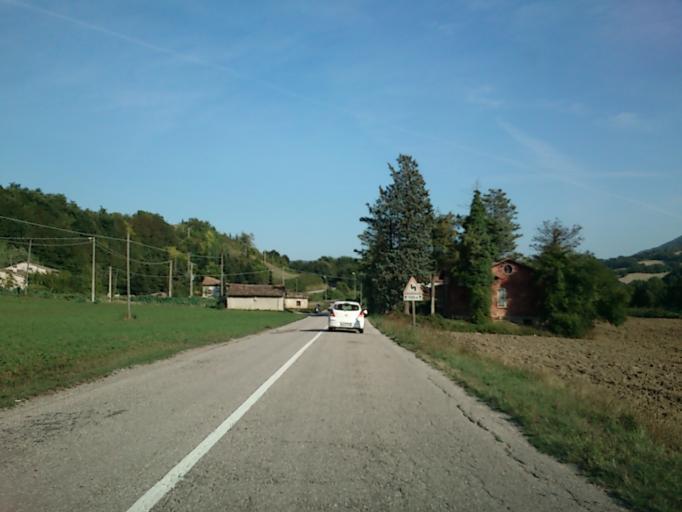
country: IT
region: The Marches
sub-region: Provincia di Pesaro e Urbino
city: Canavaccio
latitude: 43.6847
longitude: 12.7252
